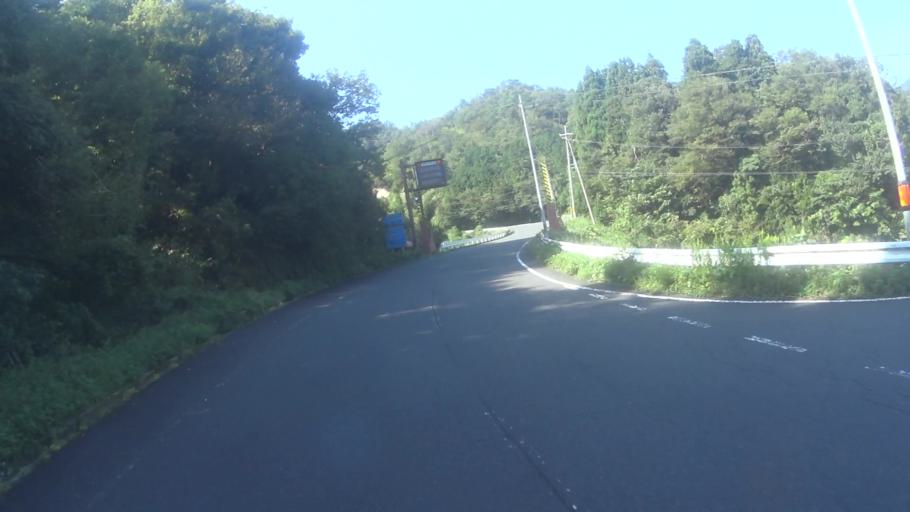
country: JP
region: Kyoto
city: Miyazu
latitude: 35.6931
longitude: 135.1473
